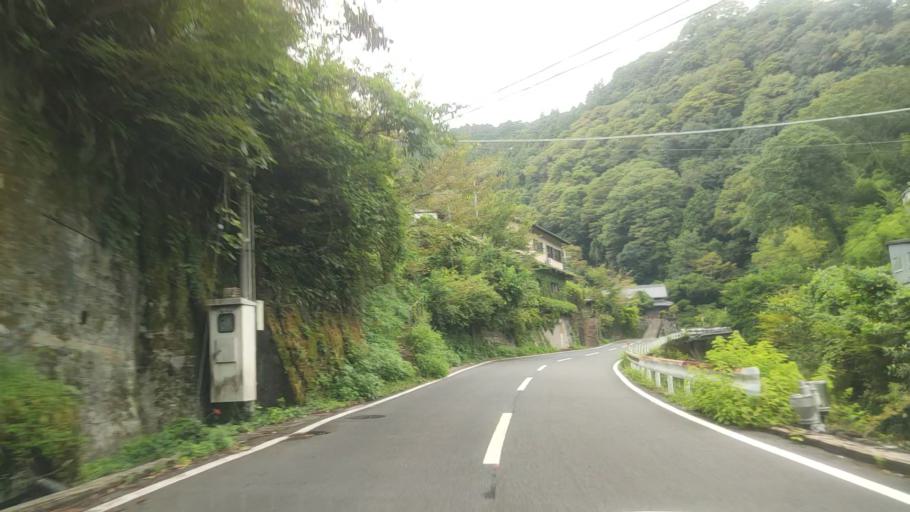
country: JP
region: Wakayama
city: Hashimoto
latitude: 34.2710
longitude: 135.5637
